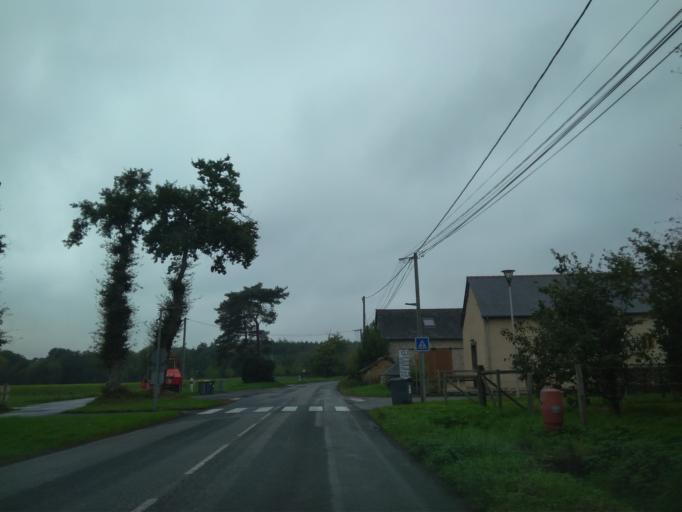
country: FR
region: Brittany
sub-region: Departement d'Ille-et-Vilaine
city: Saint-Gregoire
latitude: 48.1491
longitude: -1.6736
